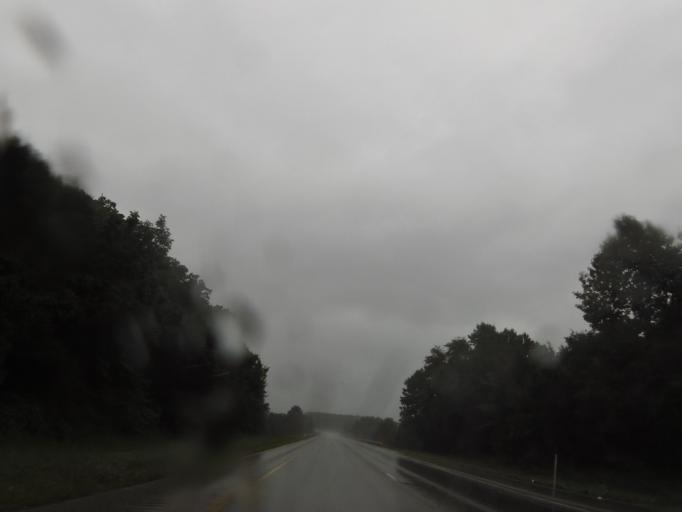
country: US
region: Illinois
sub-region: Johnson County
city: Vienna
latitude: 37.4868
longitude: -88.8930
